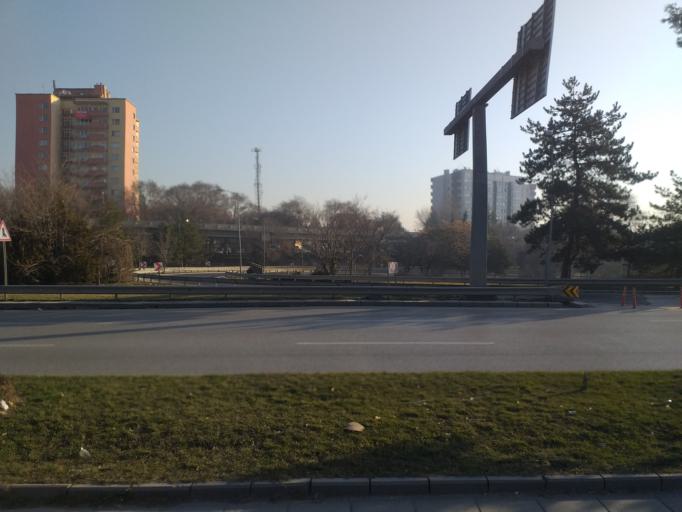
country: TR
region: Ankara
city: Ankara
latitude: 39.9551
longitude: 32.8198
